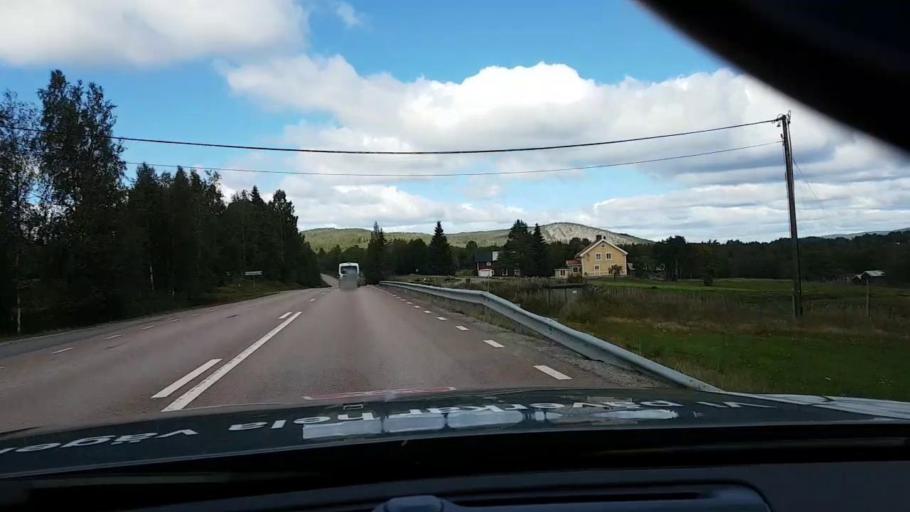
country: SE
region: Vaesternorrland
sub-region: OErnskoeldsviks Kommun
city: Bjasta
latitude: 63.3703
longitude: 18.4395
